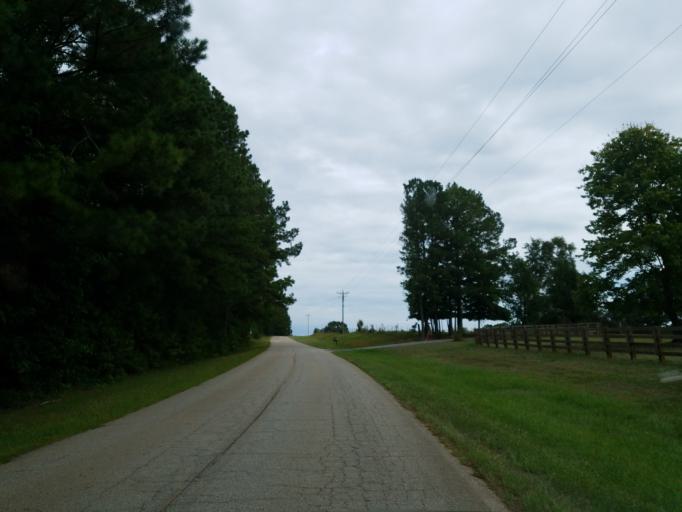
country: US
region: Georgia
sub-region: Monroe County
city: Forsyth
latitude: 32.9689
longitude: -83.9768
